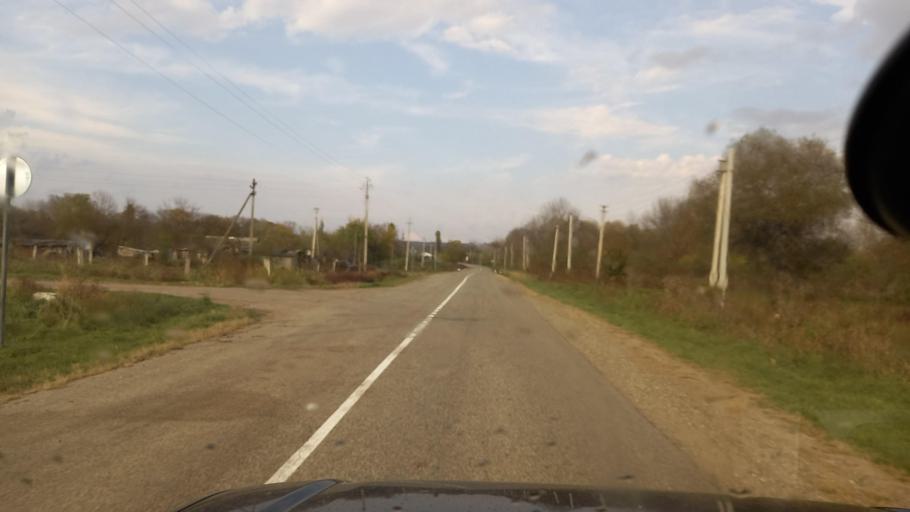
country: RU
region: Krasnodarskiy
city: Gubskaya
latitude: 44.3212
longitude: 40.6070
